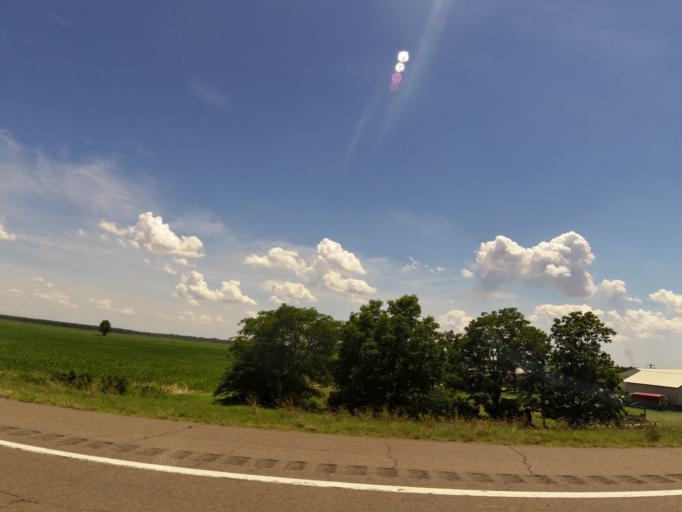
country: US
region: Missouri
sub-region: Pemiscot County
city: Caruthersville
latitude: 36.0890
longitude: -89.5676
